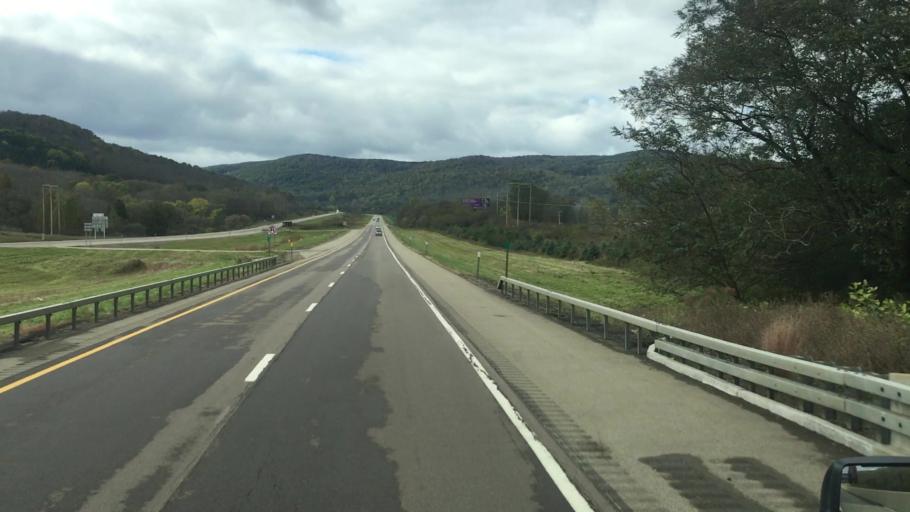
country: US
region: New York
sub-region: Allegany County
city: Cuba
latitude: 42.2181
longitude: -78.3024
